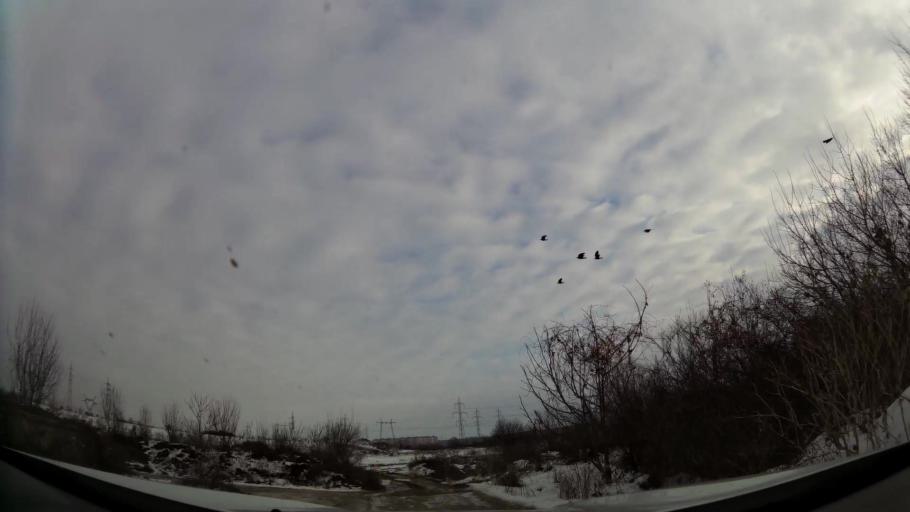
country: RO
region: Ilfov
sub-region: Comuna Popesti-Leordeni
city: Popesti-Leordeni
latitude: 44.3993
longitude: 26.1830
